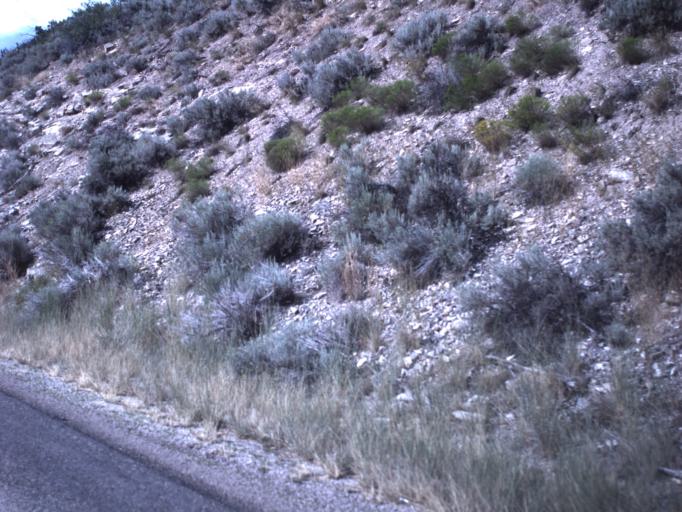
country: US
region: Utah
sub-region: Wasatch County
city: Heber
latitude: 40.4439
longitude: -111.3631
